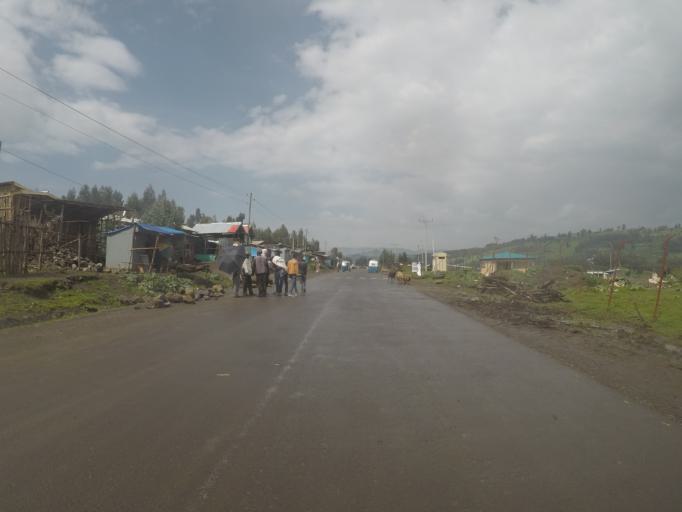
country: ET
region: Amhara
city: Debark'
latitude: 13.1250
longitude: 37.8852
